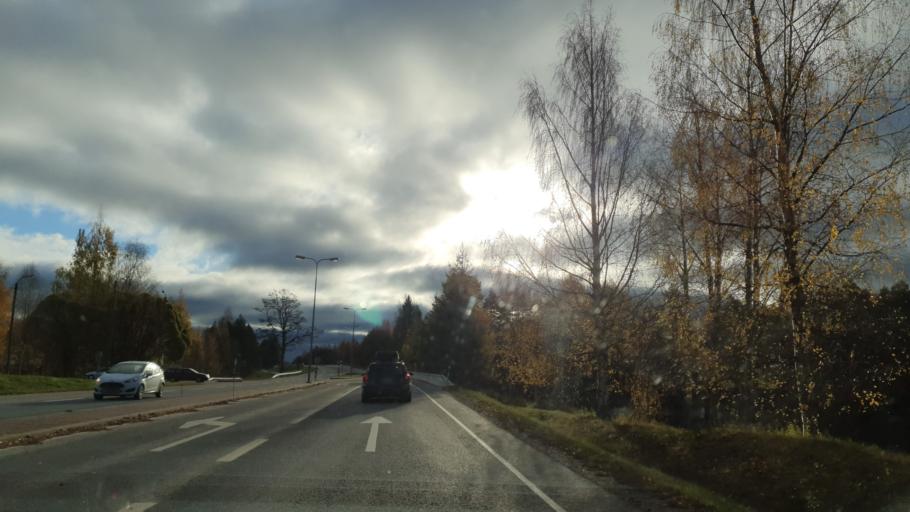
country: FI
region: Kainuu
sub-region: Kajaani
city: Vuokatti
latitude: 64.1386
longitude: 28.3326
